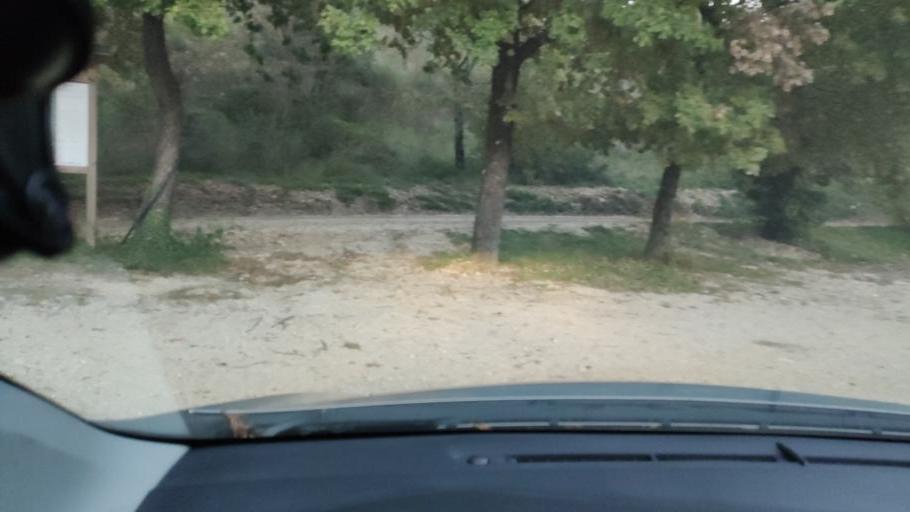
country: IT
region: Umbria
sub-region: Provincia di Terni
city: Amelia
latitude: 42.5970
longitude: 12.4331
